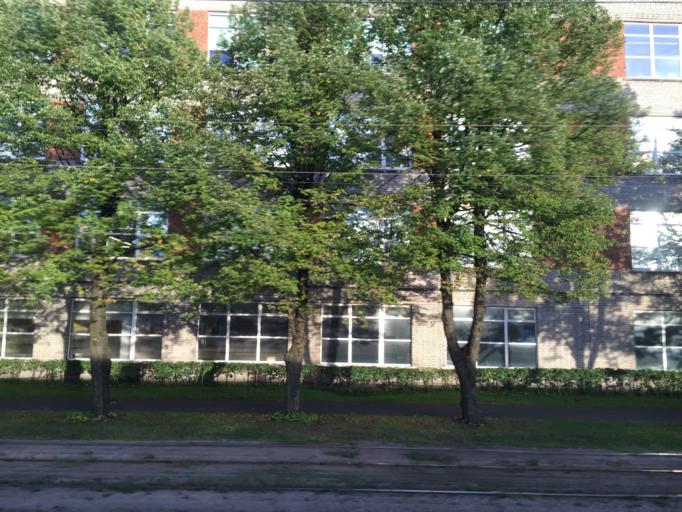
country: LV
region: Riga
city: Riga
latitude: 56.9790
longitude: 24.1154
